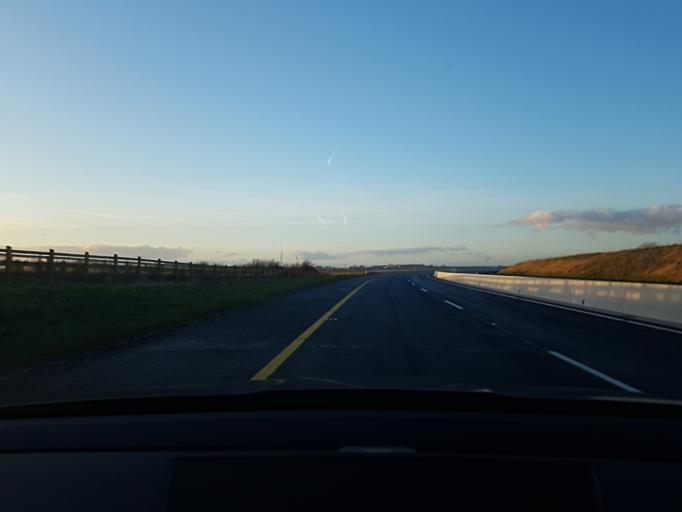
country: IE
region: Connaught
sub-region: County Galway
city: Tuam
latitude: 53.4661
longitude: -8.8591
